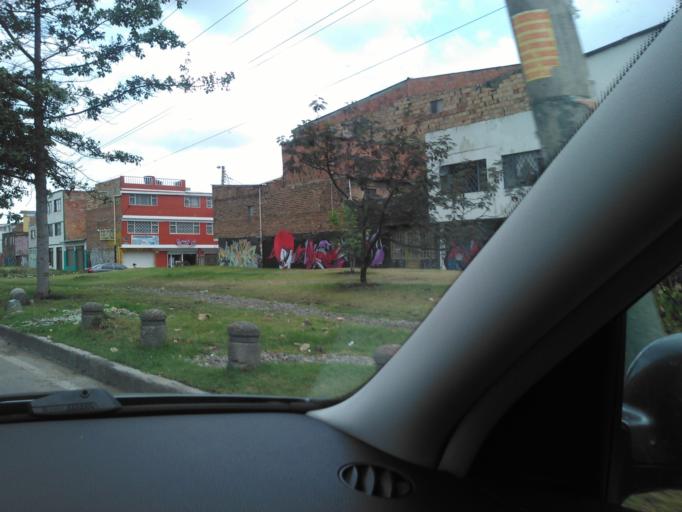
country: CO
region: Bogota D.C.
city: Bogota
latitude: 4.6133
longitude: -74.1193
